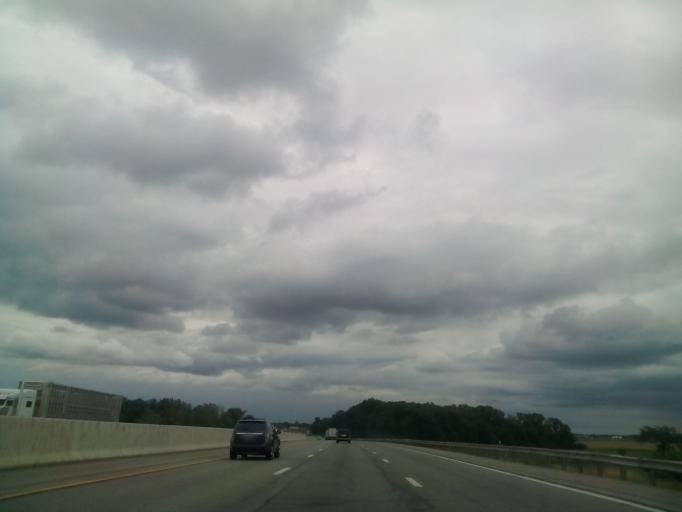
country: US
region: Ohio
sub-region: Wood County
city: Rossford
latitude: 41.5548
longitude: -83.5543
